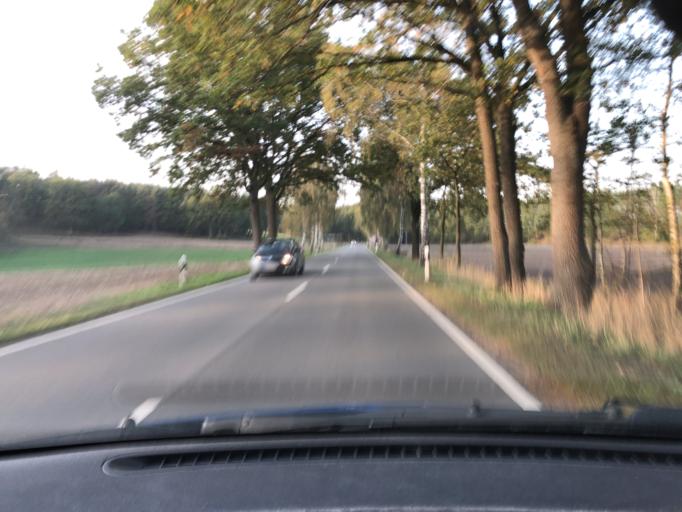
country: DE
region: Lower Saxony
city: Hitzacker
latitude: 53.1296
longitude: 11.0478
